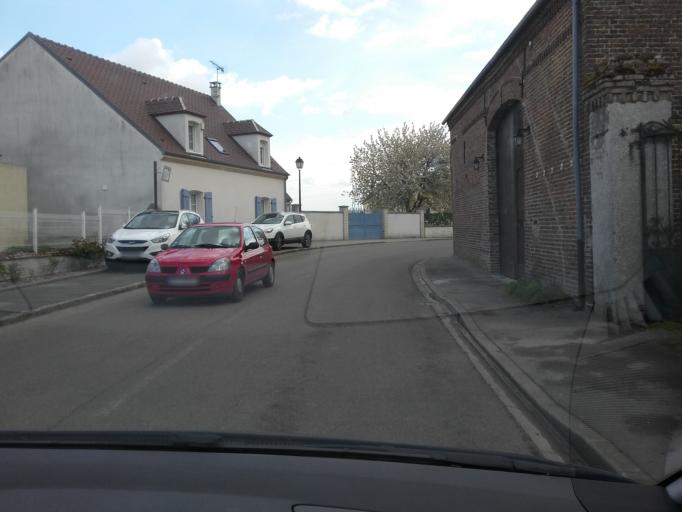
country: FR
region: Picardie
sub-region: Departement de l'Oise
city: Longueil-Sainte-Marie
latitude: 49.3717
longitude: 2.6998
